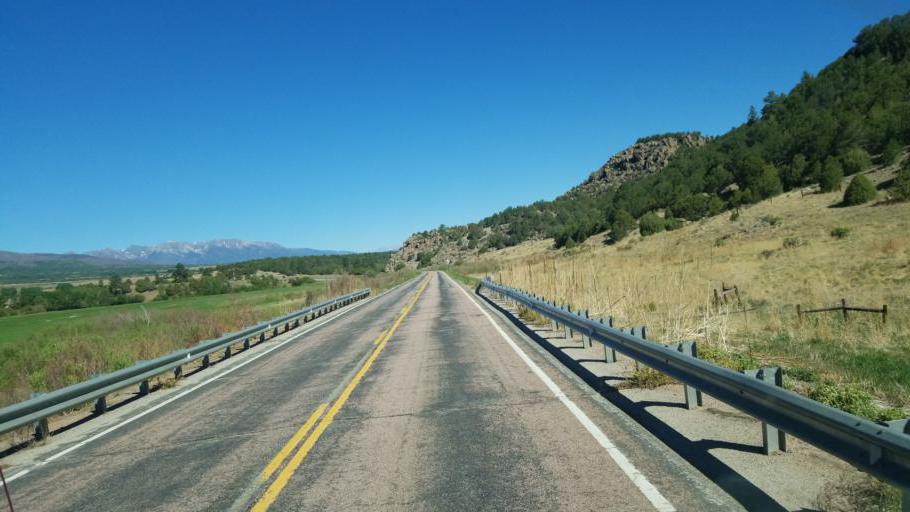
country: US
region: Colorado
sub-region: Custer County
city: Westcliffe
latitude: 38.2606
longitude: -105.5957
